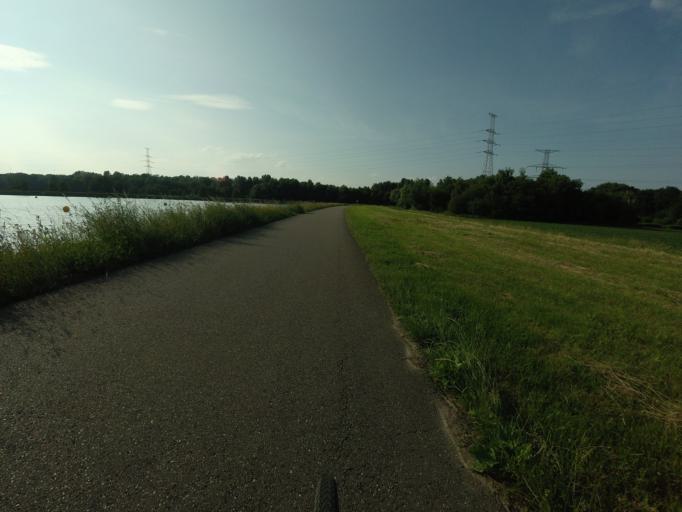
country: BE
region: Flanders
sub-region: Provincie Antwerpen
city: Zandhoven
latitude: 51.2046
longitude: 4.6174
